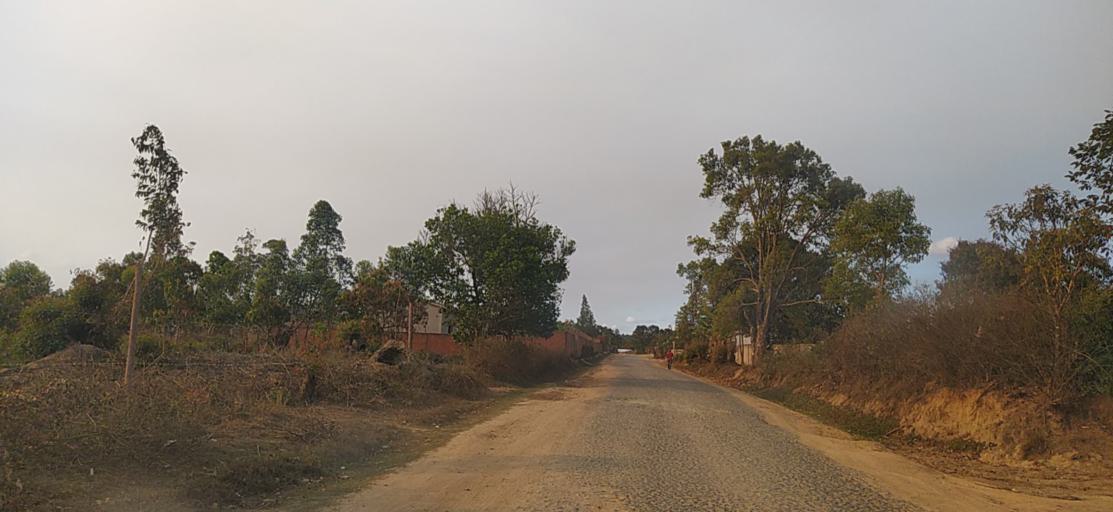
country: MG
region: Alaotra Mangoro
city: Moramanga
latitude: -18.6153
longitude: 48.2773
